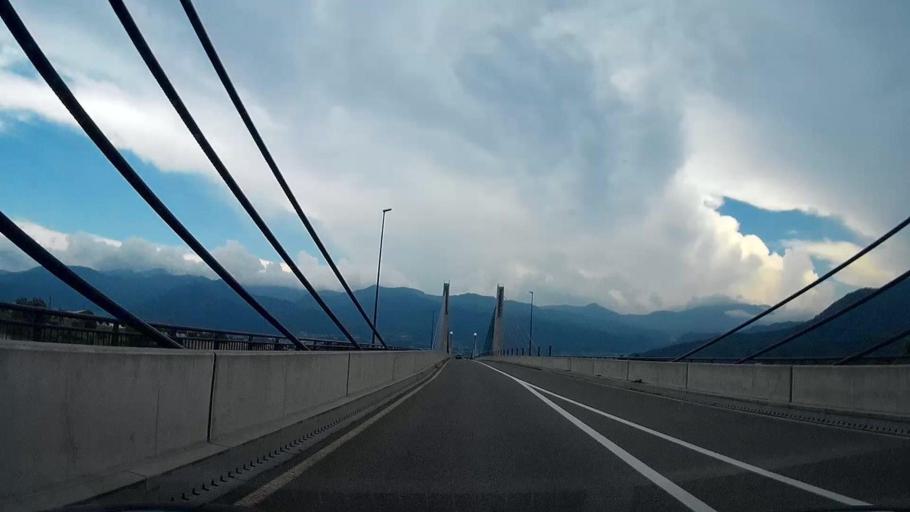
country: JP
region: Nagano
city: Iiyama
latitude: 36.8528
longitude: 138.3682
